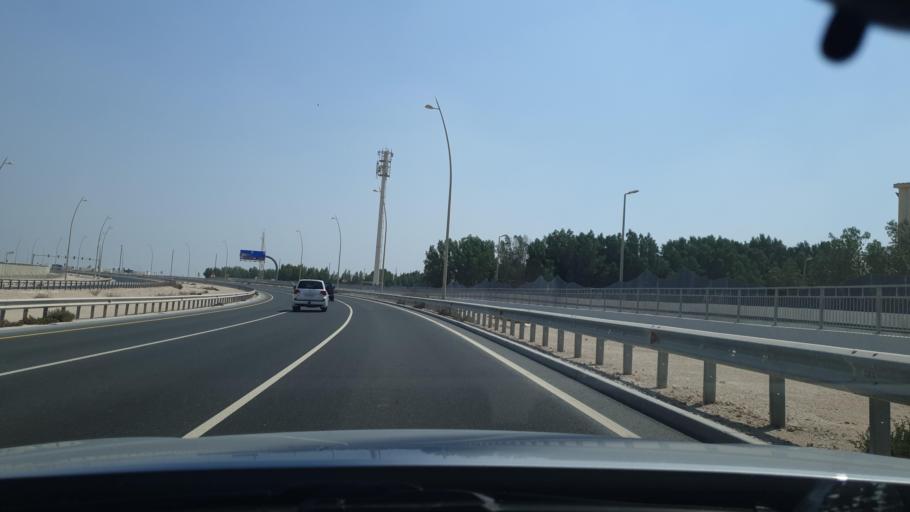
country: QA
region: Al Khawr
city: Al Khawr
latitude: 25.6607
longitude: 51.4806
